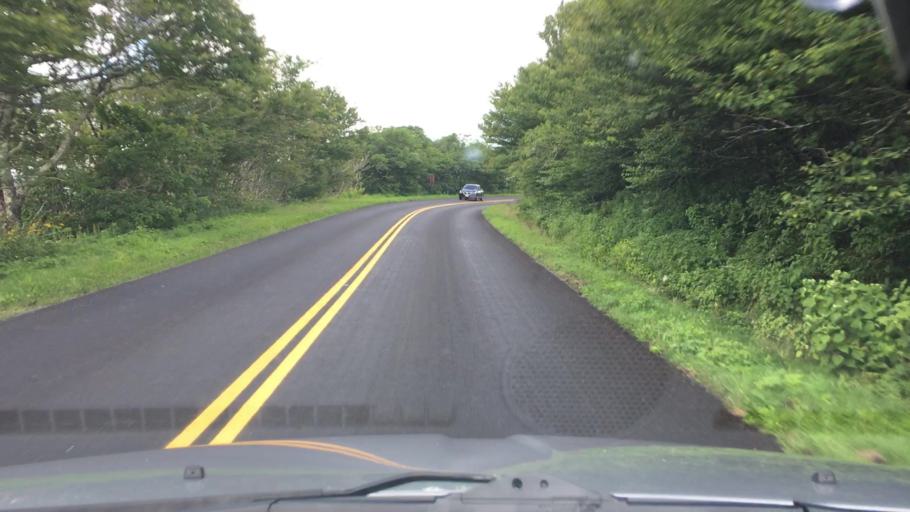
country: US
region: North Carolina
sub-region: Buncombe County
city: Black Mountain
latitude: 35.7118
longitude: -82.3642
